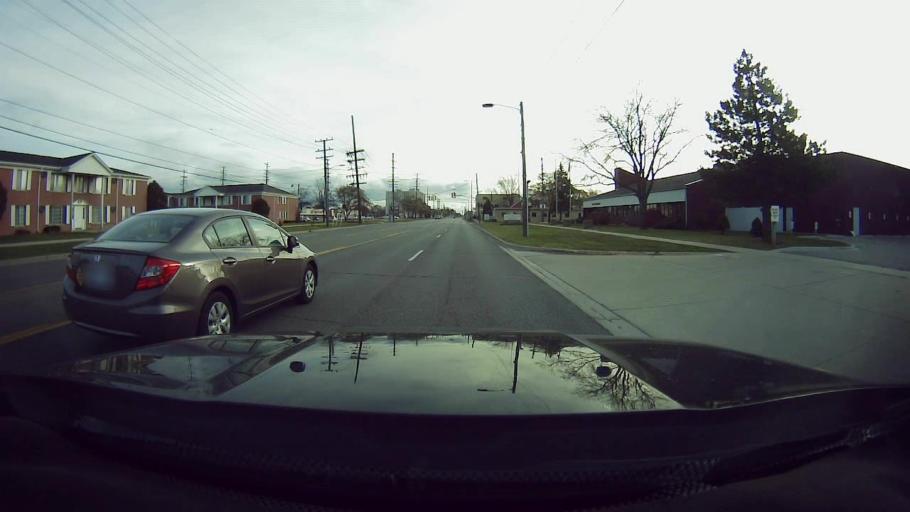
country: US
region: Michigan
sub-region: Macomb County
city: Warren
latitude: 42.4774
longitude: -83.0328
